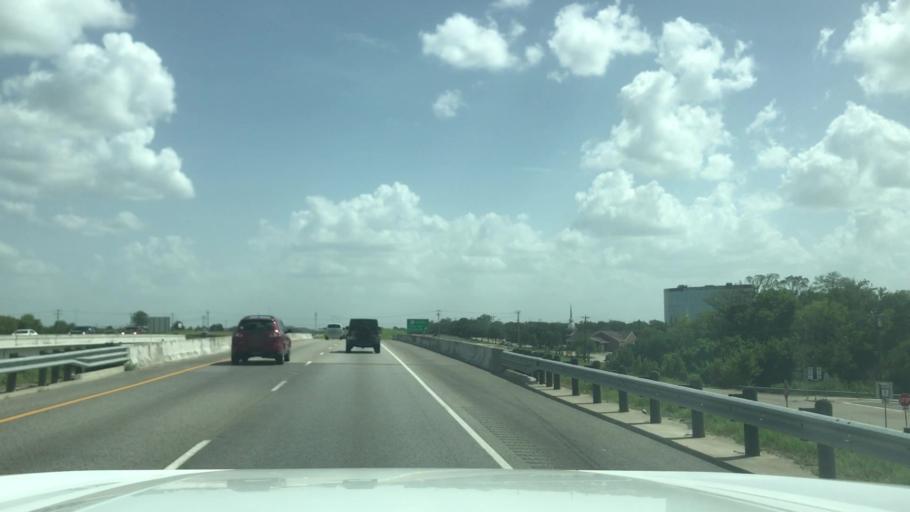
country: US
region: Texas
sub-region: Brazos County
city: College Station
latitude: 30.6040
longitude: -96.2903
